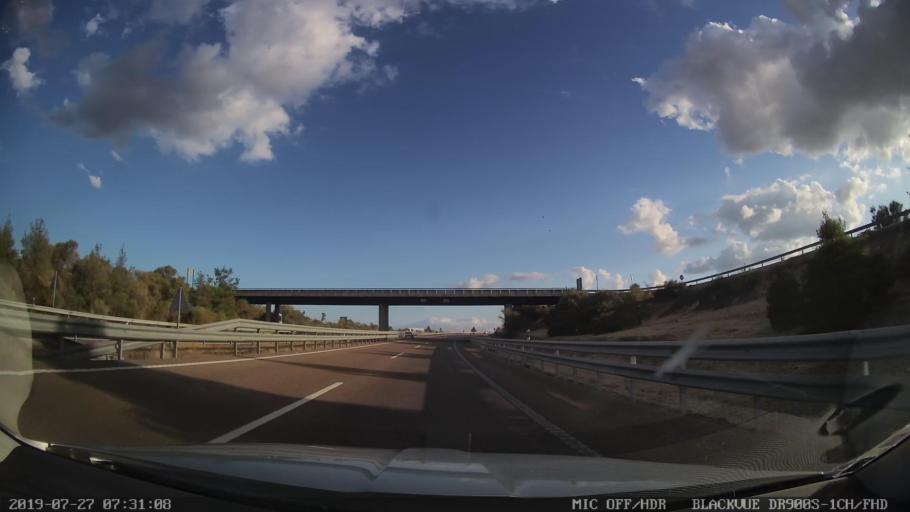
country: ES
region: Extremadura
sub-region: Provincia de Caceres
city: Escurial
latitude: 39.1761
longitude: -5.8975
